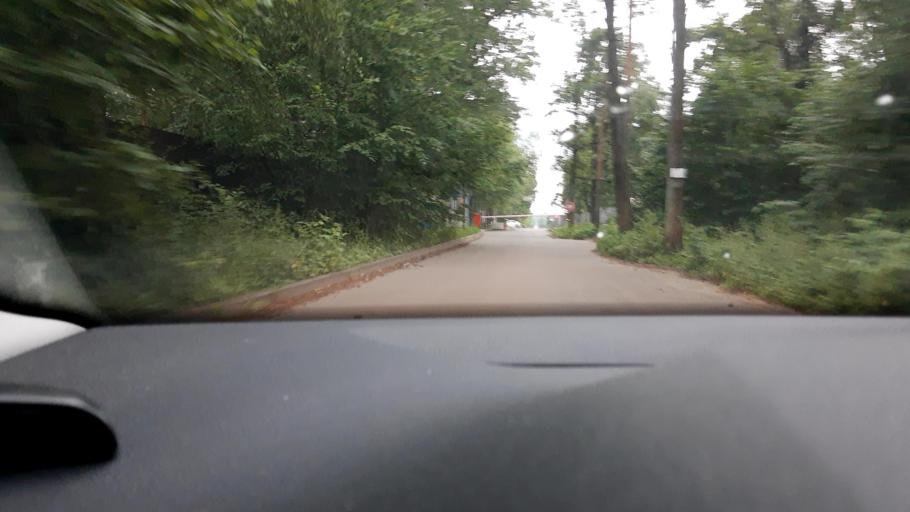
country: RU
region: Moskovskaya
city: Novopodrezkovo
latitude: 55.8923
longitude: 37.3397
